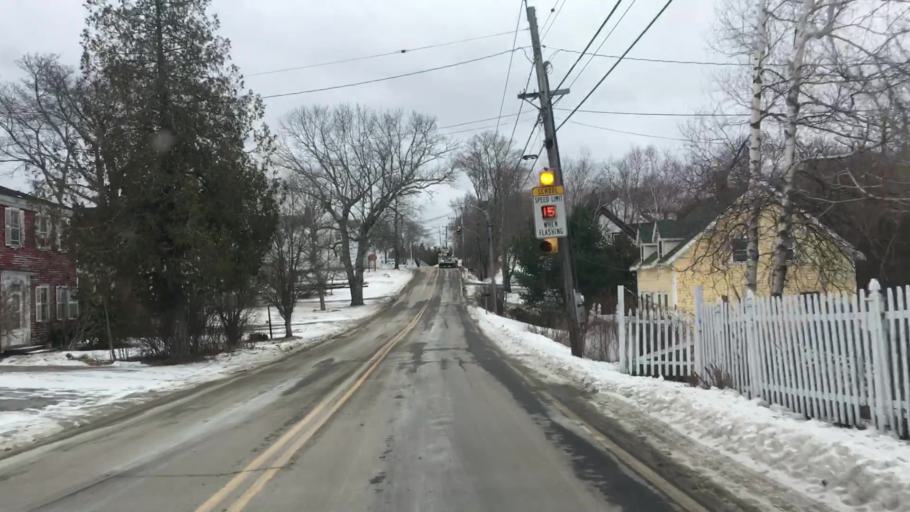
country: US
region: Maine
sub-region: Washington County
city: East Machias
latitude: 44.7360
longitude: -67.3886
